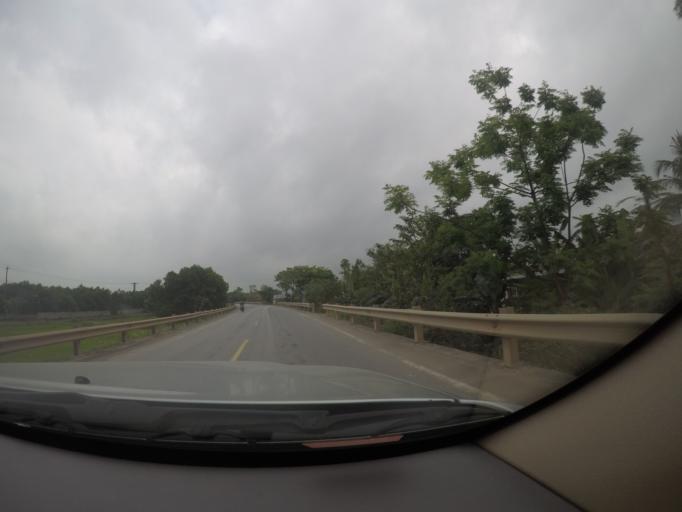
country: VN
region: Quang Binh
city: Kien Giang
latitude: 17.2055
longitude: 106.7156
